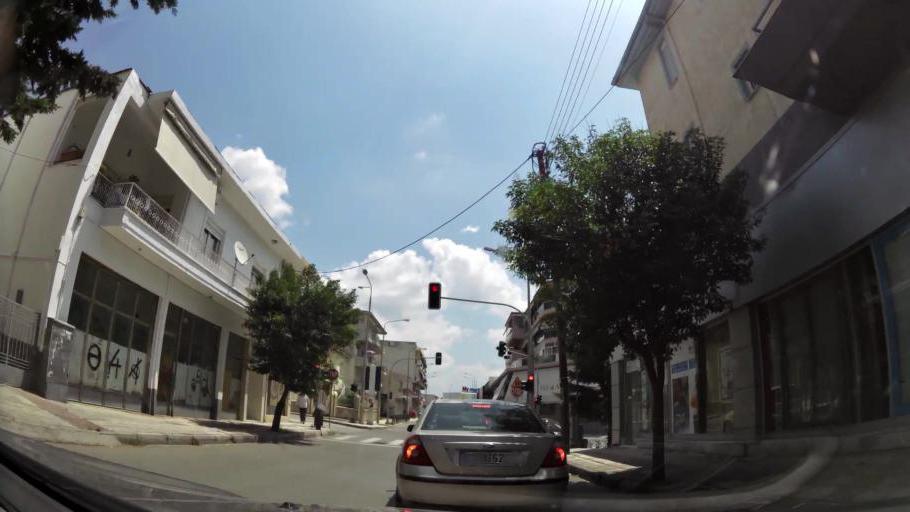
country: GR
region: West Macedonia
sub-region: Nomos Kozanis
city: Kozani
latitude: 40.2991
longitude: 21.7959
